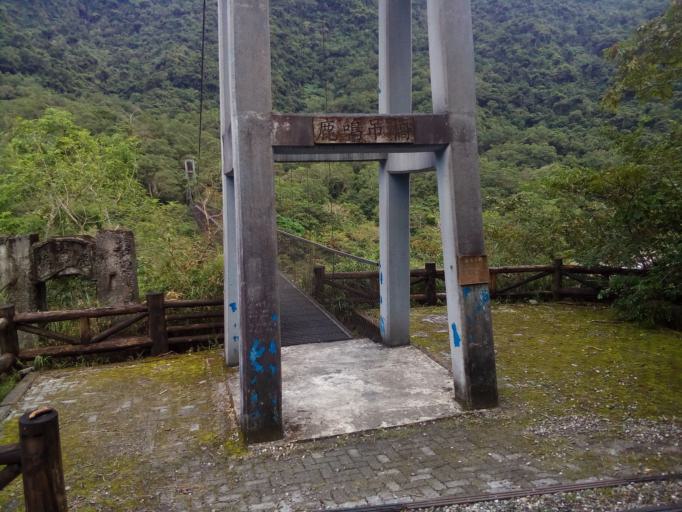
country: TW
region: Taiwan
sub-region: Taitung
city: Taitung
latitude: 23.3179
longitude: 121.2540
